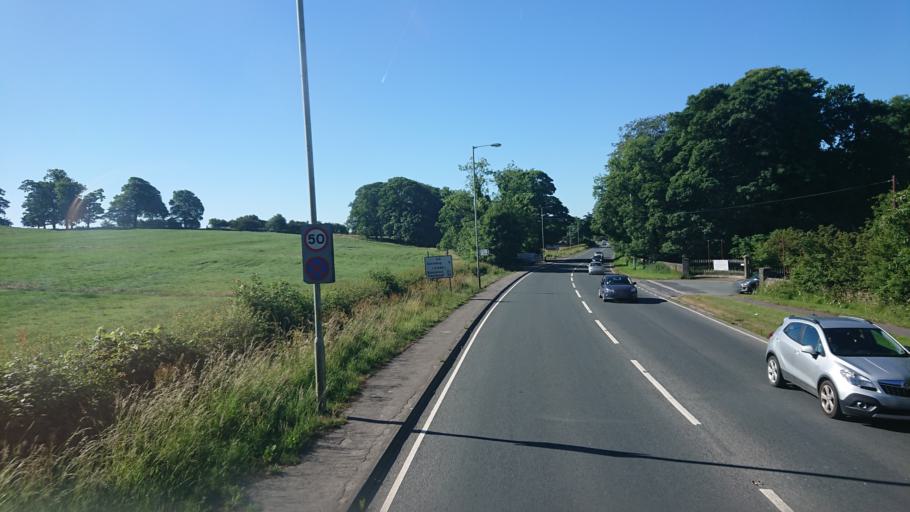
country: GB
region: England
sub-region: Lancashire
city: Galgate
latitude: 53.9796
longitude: -2.7849
